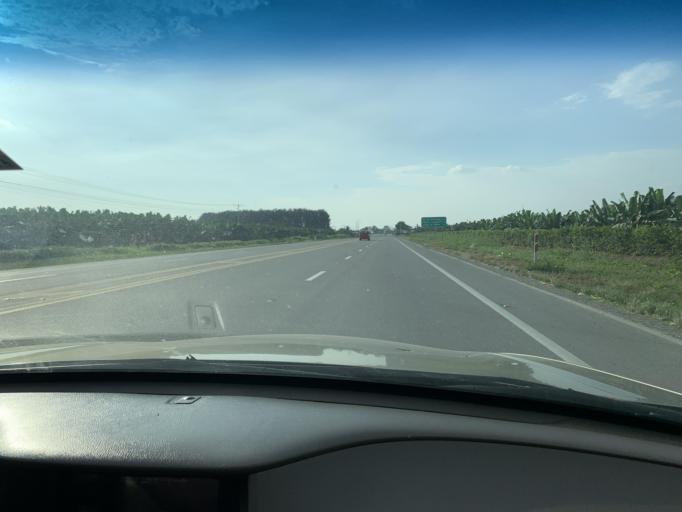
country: EC
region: Guayas
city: Coronel Marcelino Mariduena
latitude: -2.2642
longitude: -79.5465
